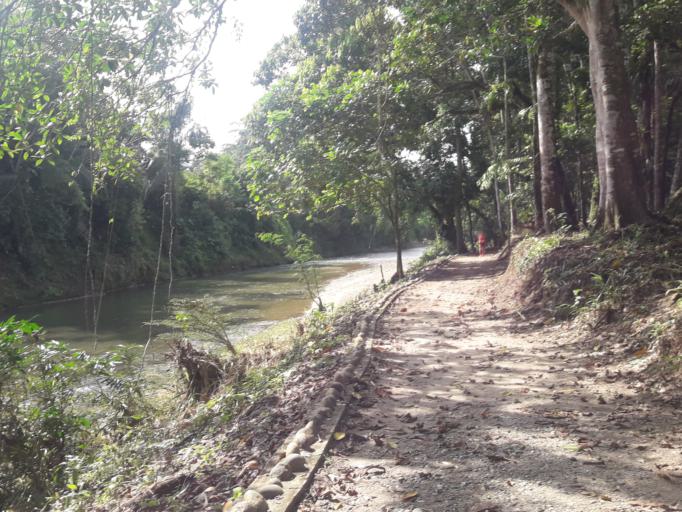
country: EC
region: Napo
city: Tena
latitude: -0.9949
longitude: -77.8186
